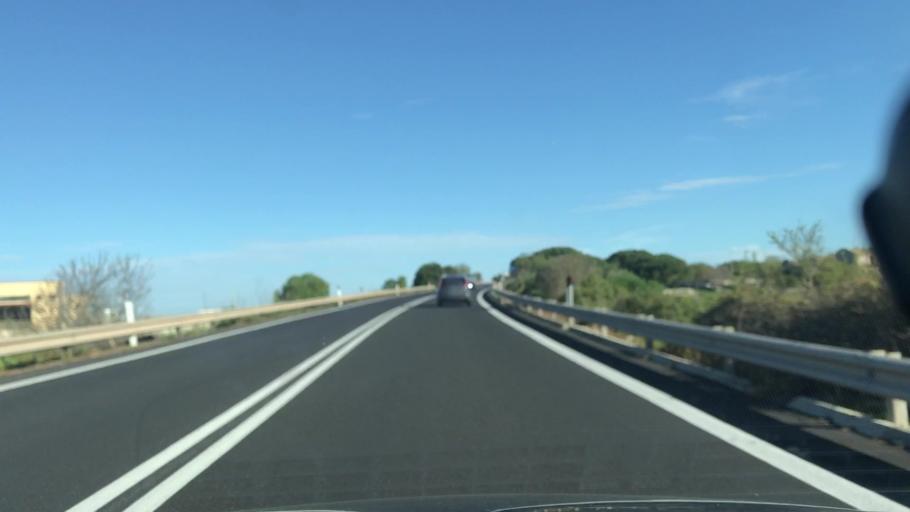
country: IT
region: Sicily
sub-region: Ragusa
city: Comiso
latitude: 36.9359
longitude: 14.6515
